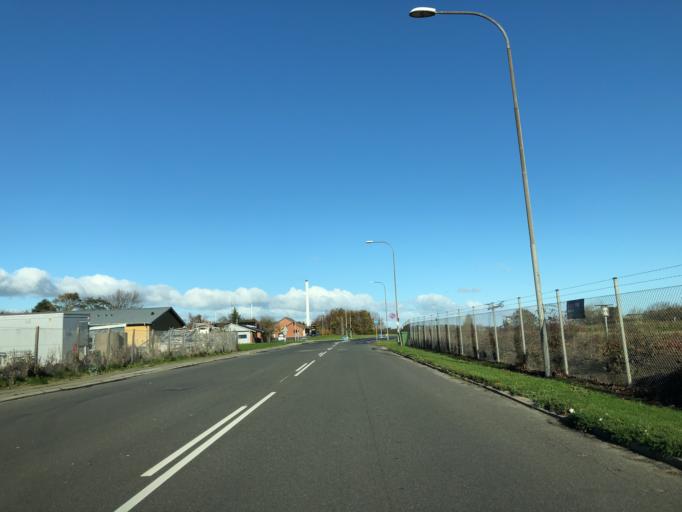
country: DK
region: Central Jutland
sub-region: Holstebro Kommune
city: Holstebro
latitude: 56.3840
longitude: 8.6209
